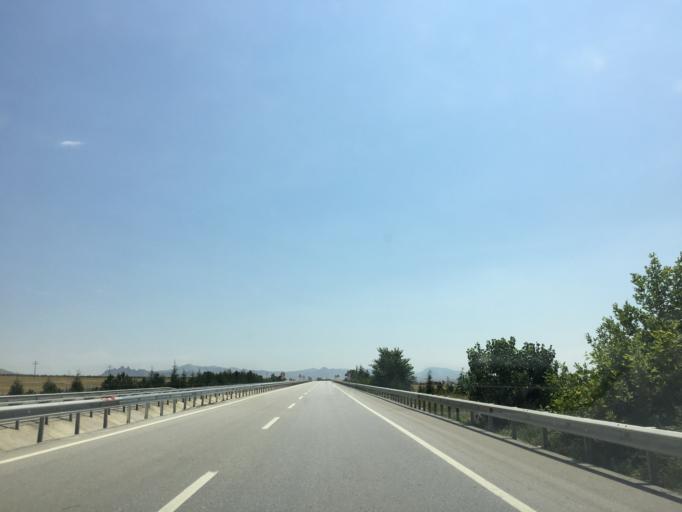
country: TR
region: Eskisehir
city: Sivrihisar
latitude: 39.4590
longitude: 31.3864
